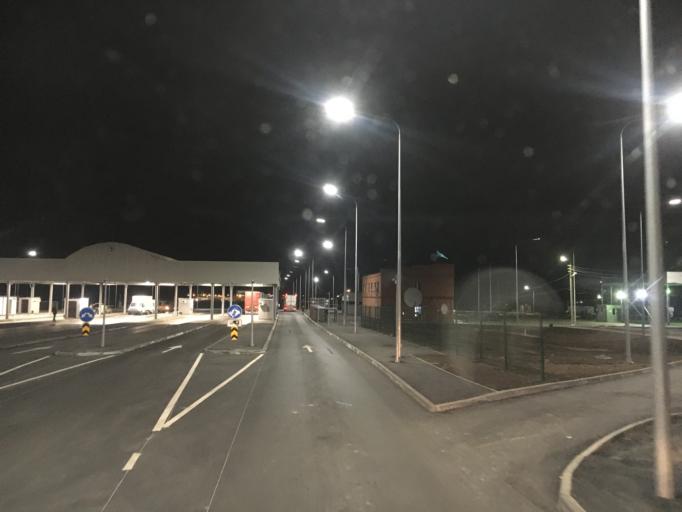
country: KZ
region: Batys Qazaqstan
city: Peremetnoe
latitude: 51.6653
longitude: 51.0058
